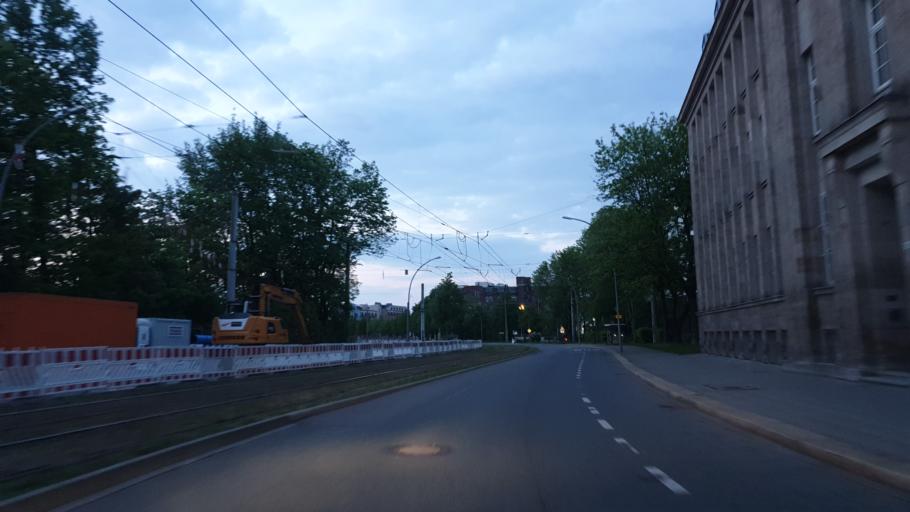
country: DE
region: Saxony
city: Chemnitz
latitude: 50.8200
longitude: 12.9159
